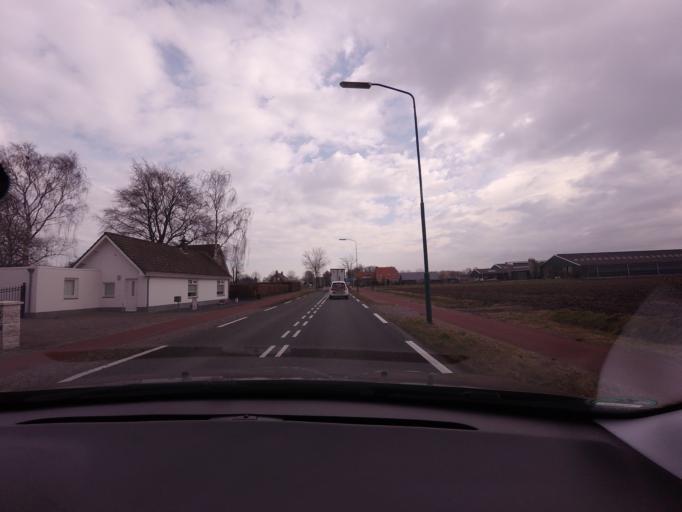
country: NL
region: North Brabant
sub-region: Gemeente Dongen
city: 's Gravenmoer
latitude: 51.6482
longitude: 5.0082
